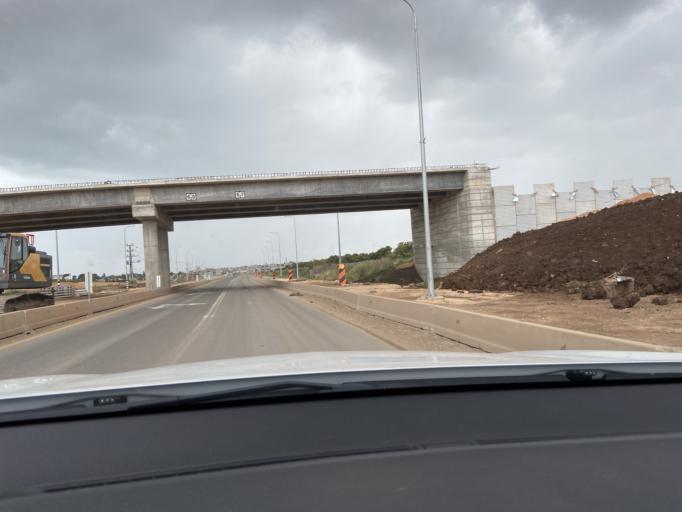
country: IL
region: Northern District
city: El Mazra`a
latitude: 32.9778
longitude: 35.1141
